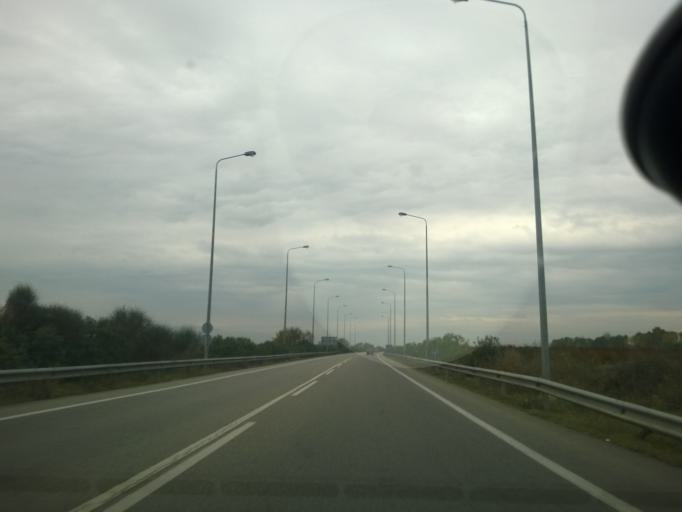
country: GR
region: Central Macedonia
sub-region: Nomos Pellis
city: Karyotissa
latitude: 40.7795
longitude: 22.3094
